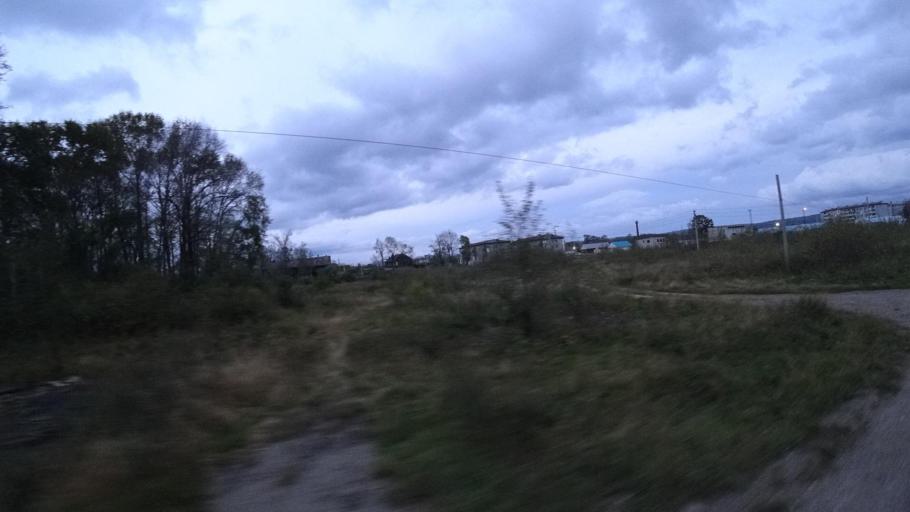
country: RU
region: Jewish Autonomous Oblast
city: Izvestkovyy
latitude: 48.9833
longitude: 131.5482
